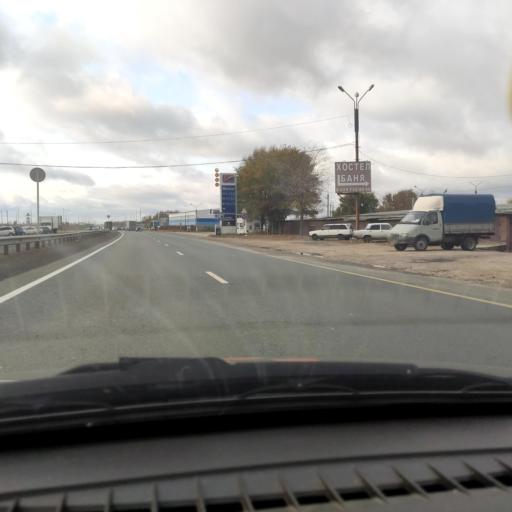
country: RU
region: Samara
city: Tol'yatti
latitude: 53.5721
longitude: 49.4649
